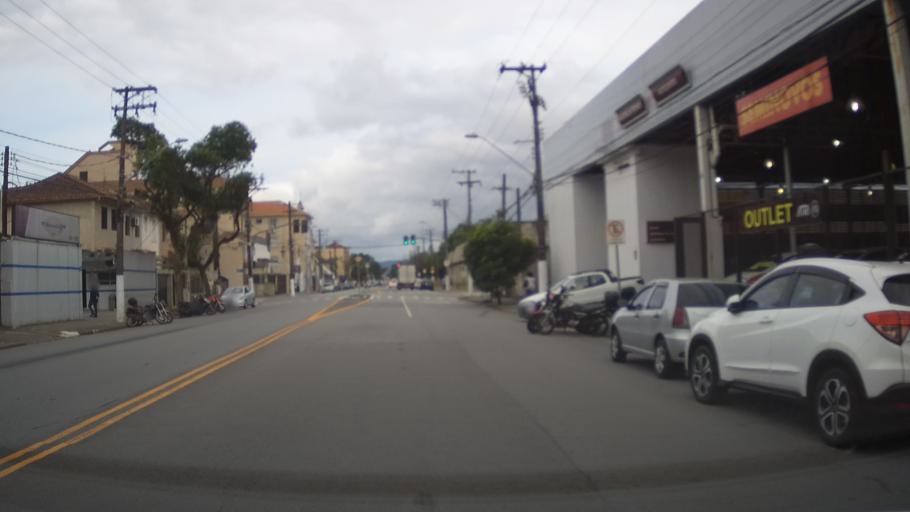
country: BR
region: Sao Paulo
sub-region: Santos
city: Santos
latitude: -23.9562
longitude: -46.3181
